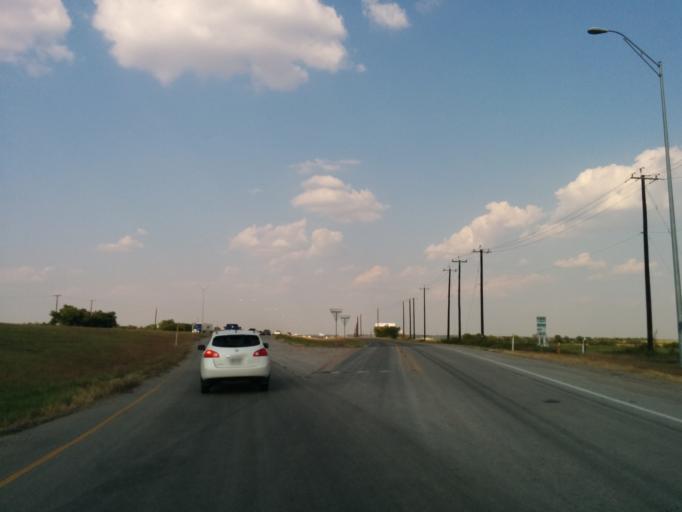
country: US
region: Texas
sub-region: Bexar County
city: Converse
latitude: 29.4653
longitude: -98.2905
